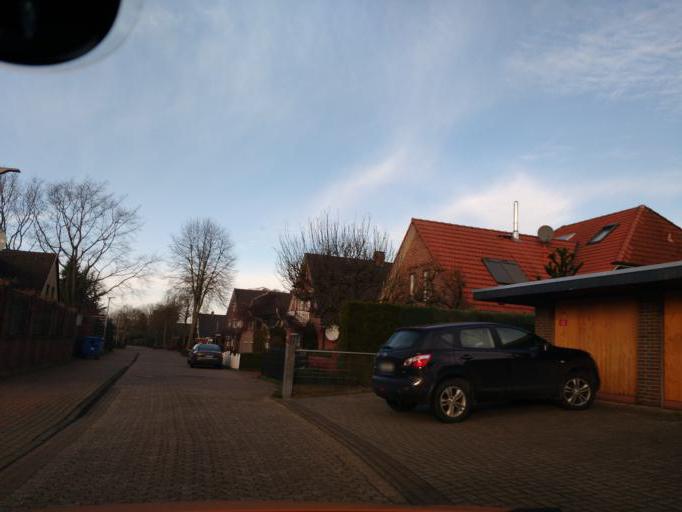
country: DE
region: Lower Saxony
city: Hude
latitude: 53.1099
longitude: 8.4660
